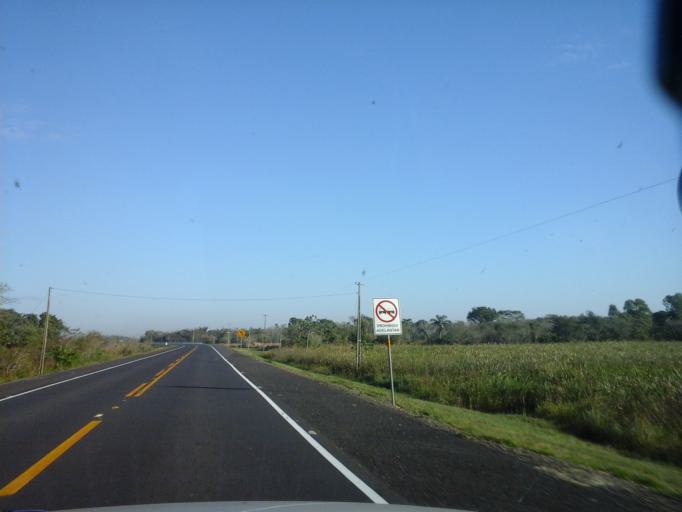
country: PY
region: Neembucu
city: Pilar
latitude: -26.8752
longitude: -57.8992
